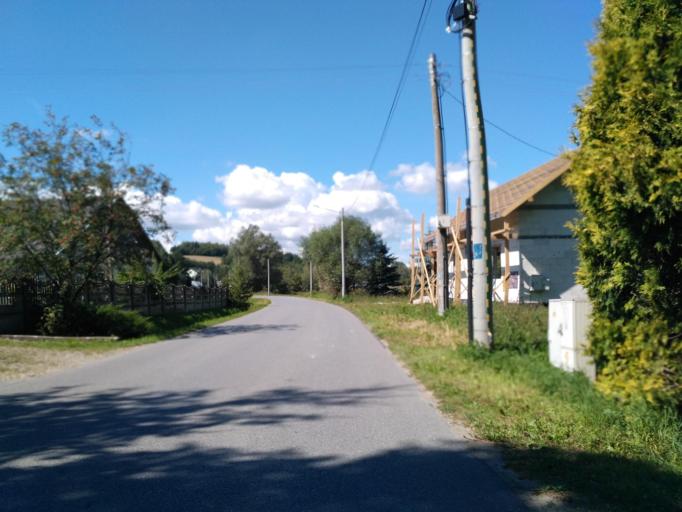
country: PL
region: Subcarpathian Voivodeship
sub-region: Powiat jasielski
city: Skolyszyn
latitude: 49.7975
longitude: 21.3193
